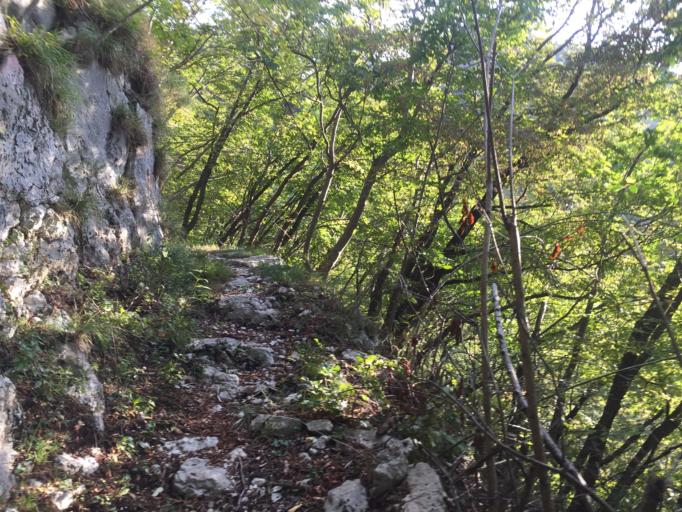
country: IT
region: Friuli Venezia Giulia
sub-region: Provincia di Udine
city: Venzone
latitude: 46.3436
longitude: 13.1834
